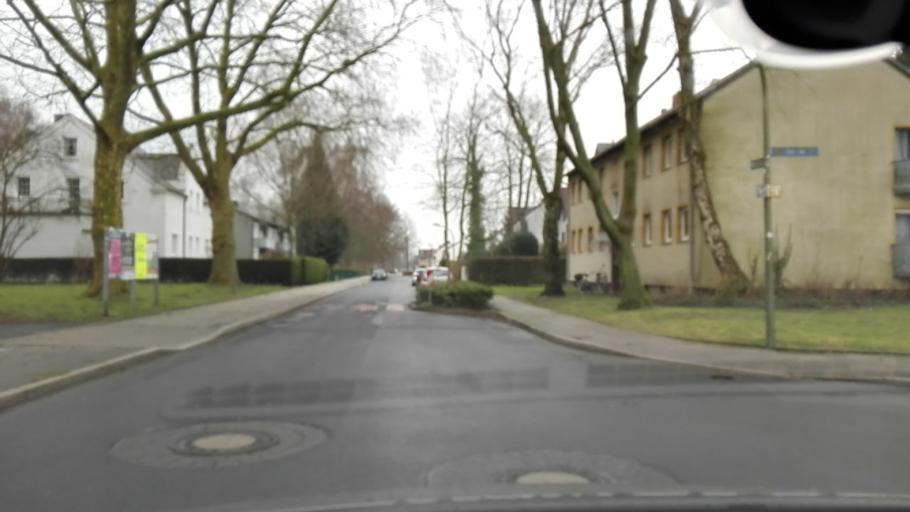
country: DE
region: North Rhine-Westphalia
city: Kamen
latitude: 51.5828
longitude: 7.7128
